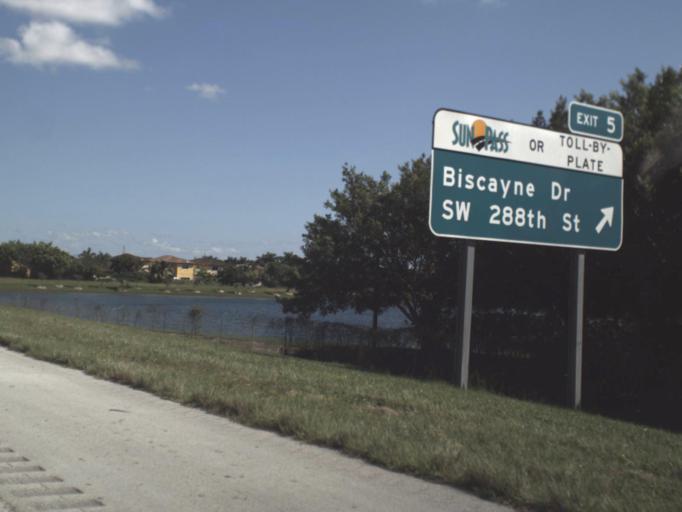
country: US
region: Florida
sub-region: Miami-Dade County
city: Leisure City
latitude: 25.4923
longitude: -80.4193
